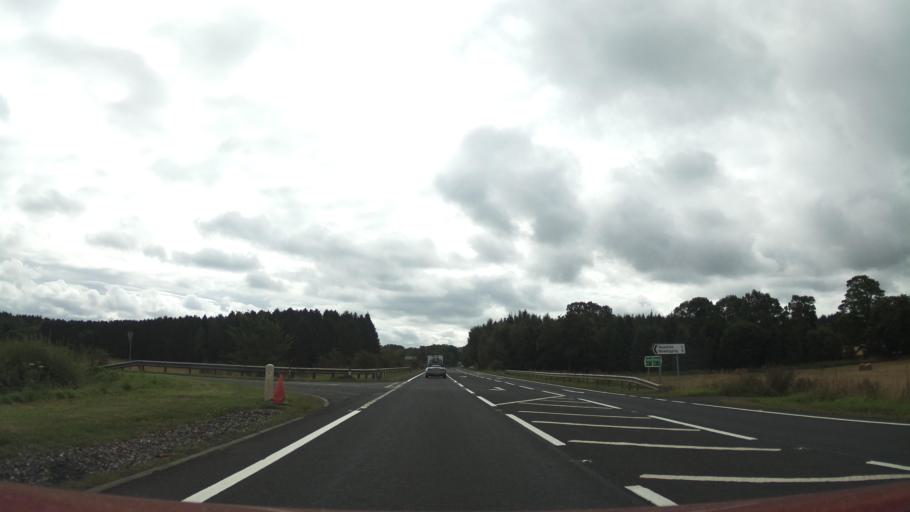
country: GB
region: Scotland
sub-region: The Scottish Borders
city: Lauder
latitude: 55.7380
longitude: -2.7665
